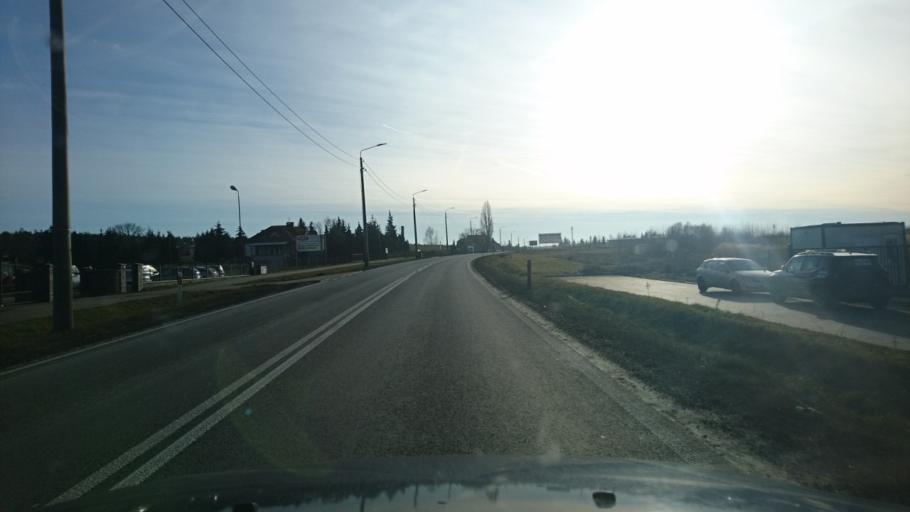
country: PL
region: Greater Poland Voivodeship
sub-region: Powiat ostrzeszowski
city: Ostrzeszow
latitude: 51.4431
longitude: 17.9131
